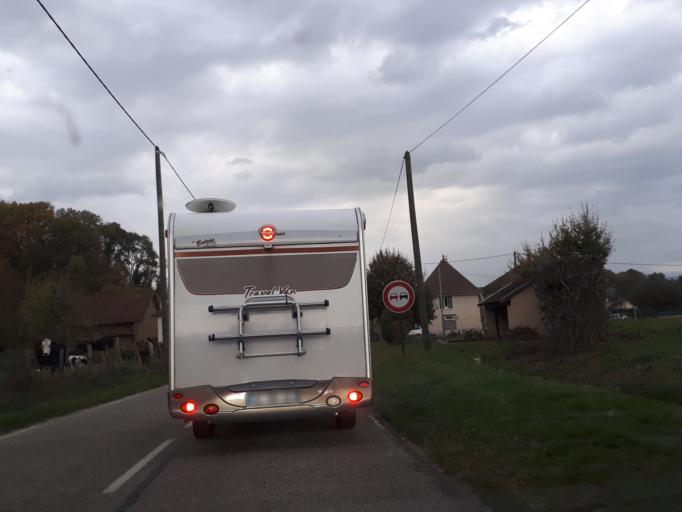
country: FR
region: Rhone-Alpes
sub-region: Departement de l'Isere
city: Curtin
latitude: 45.6317
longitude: 5.4828
